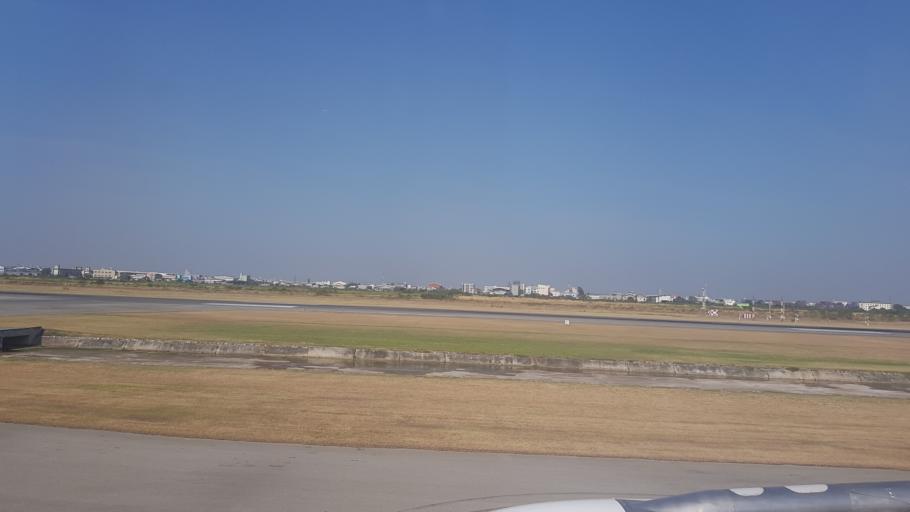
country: TH
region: Bangkok
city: Lat Krabang
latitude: 13.6727
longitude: 100.7369
